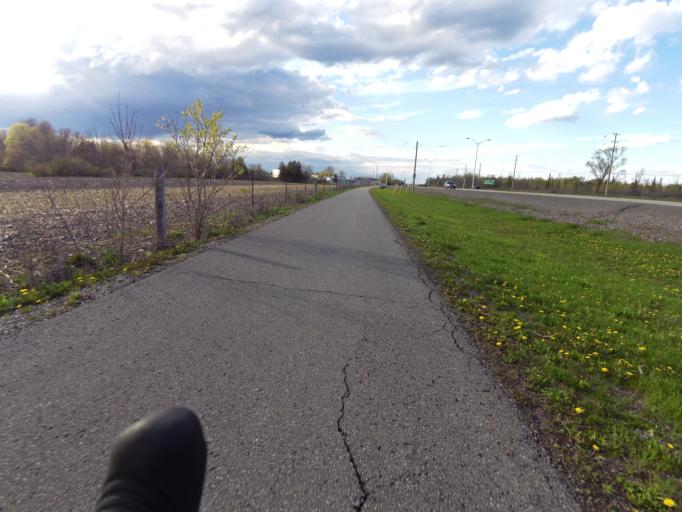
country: CA
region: Ontario
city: Ottawa
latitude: 45.3134
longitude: -75.6860
